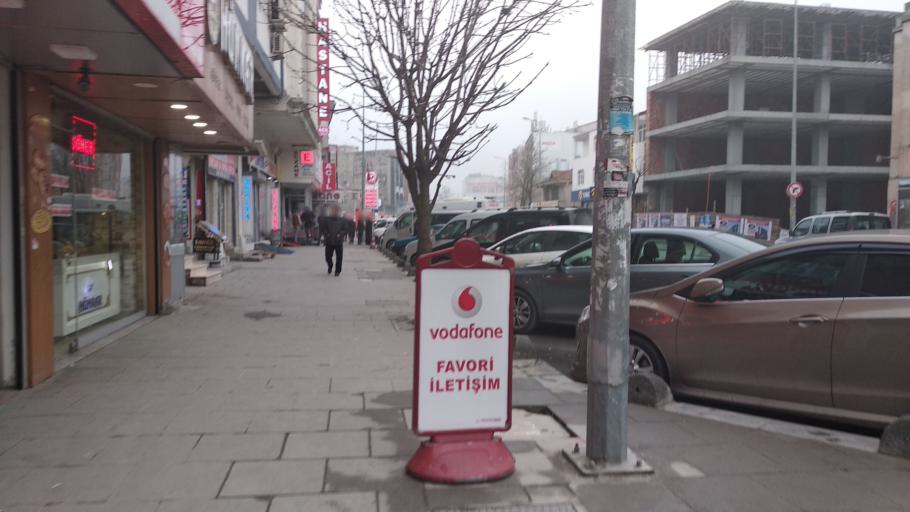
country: TR
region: Istanbul
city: Basaksehir
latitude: 41.1819
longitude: 28.7438
